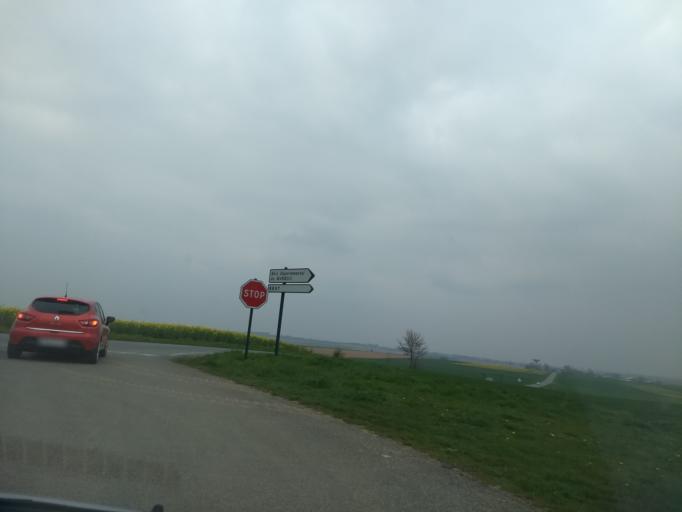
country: FR
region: Nord-Pas-de-Calais
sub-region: Departement du Pas-de-Calais
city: Maroeuil
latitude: 50.3381
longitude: 2.7054
